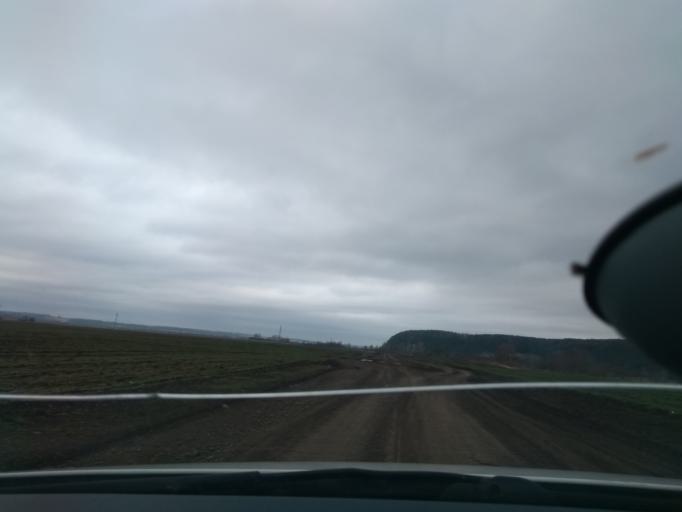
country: RU
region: Perm
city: Orda
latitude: 57.2543
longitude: 56.6256
